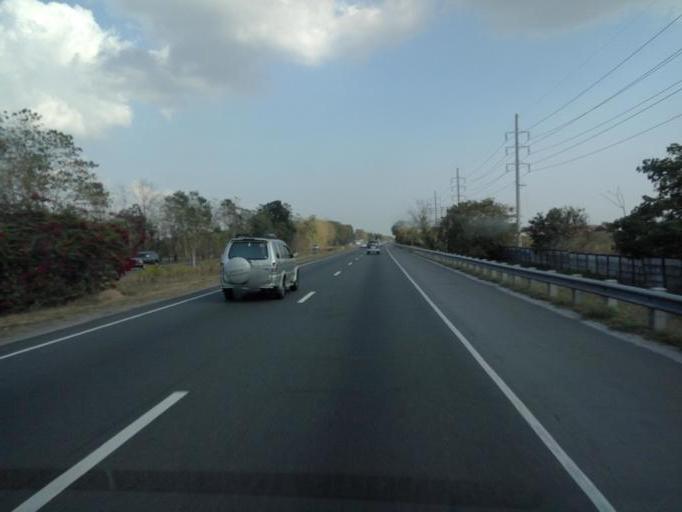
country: PH
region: Central Luzon
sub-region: Province of Pampanga
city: Acli
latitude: 15.1174
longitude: 120.6549
